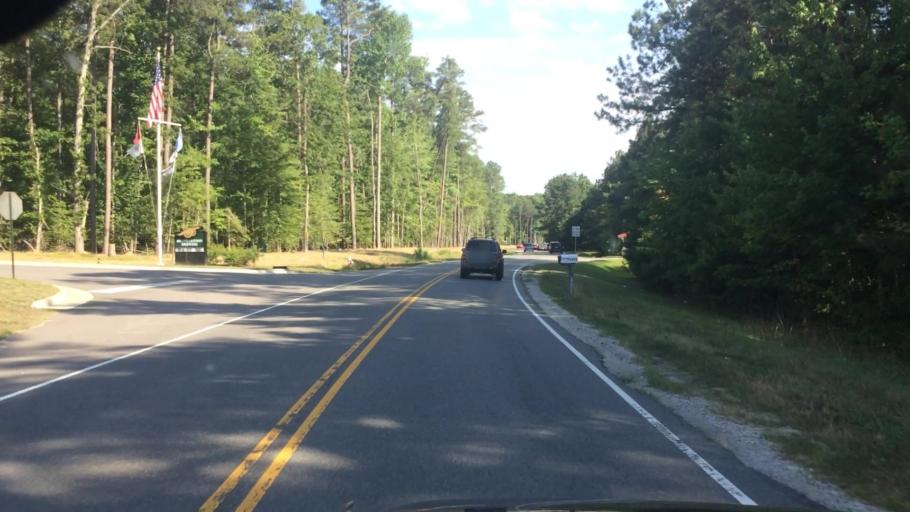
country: US
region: Virginia
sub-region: James City County
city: Williamsburg
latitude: 37.3159
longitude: -76.7311
